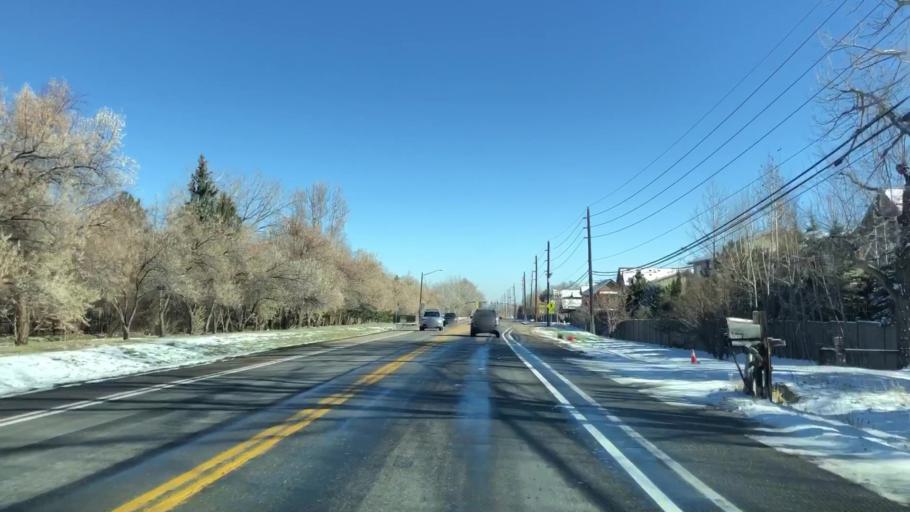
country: US
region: Colorado
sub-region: Boulder County
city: Boulder
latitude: 40.0511
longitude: -105.2485
